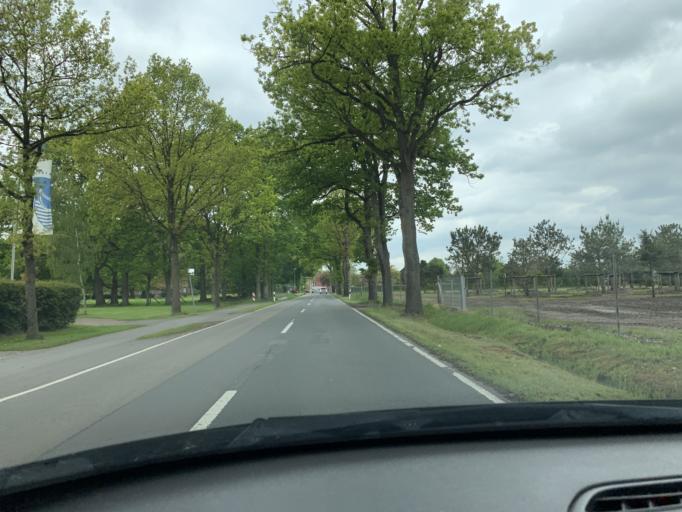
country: DE
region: Lower Saxony
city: Bad Zwischenahn
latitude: 53.2137
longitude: 8.0250
